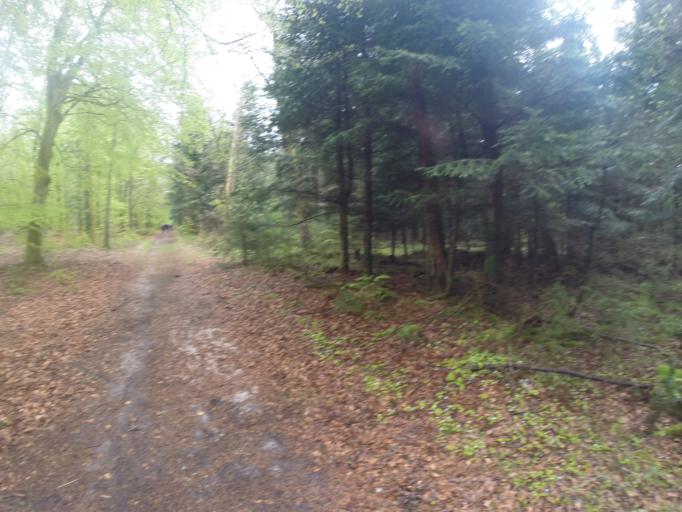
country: DK
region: North Denmark
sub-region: Thisted Kommune
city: Hanstholm
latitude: 57.0317
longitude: 8.5833
